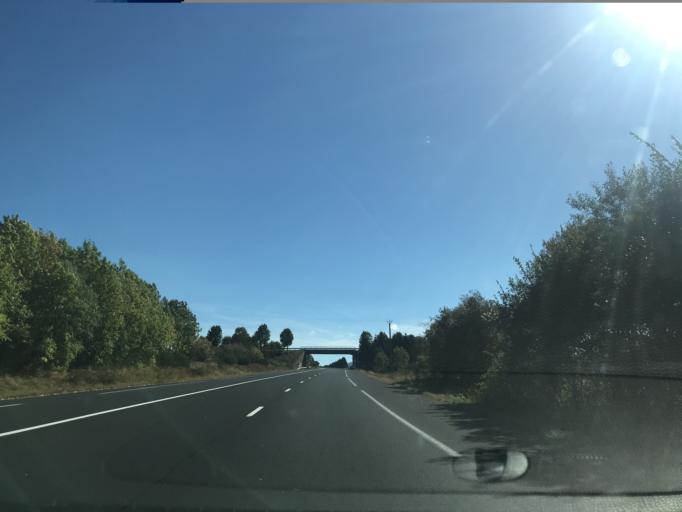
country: FR
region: Auvergne
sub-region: Departement du Puy-de-Dome
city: La Bourboule
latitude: 45.6649
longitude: 2.7445
